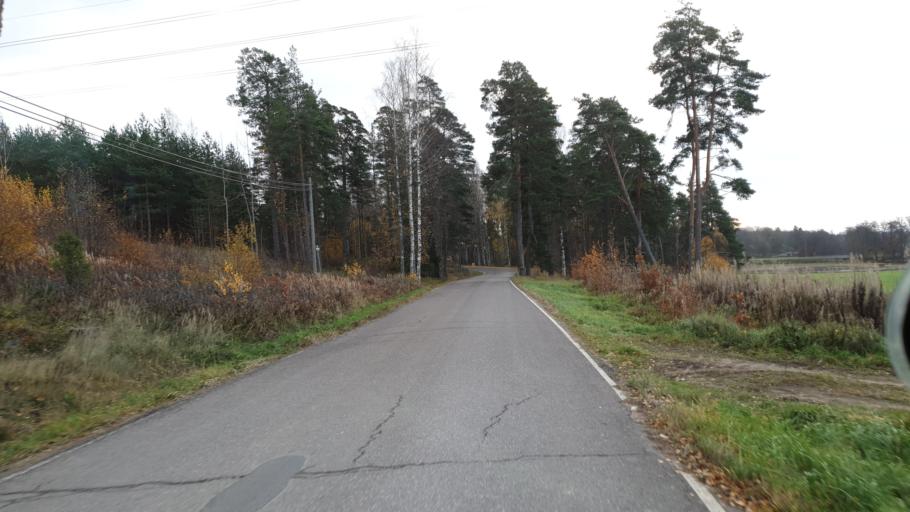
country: FI
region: Uusimaa
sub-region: Helsinki
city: Siuntio
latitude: 60.1035
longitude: 24.2944
